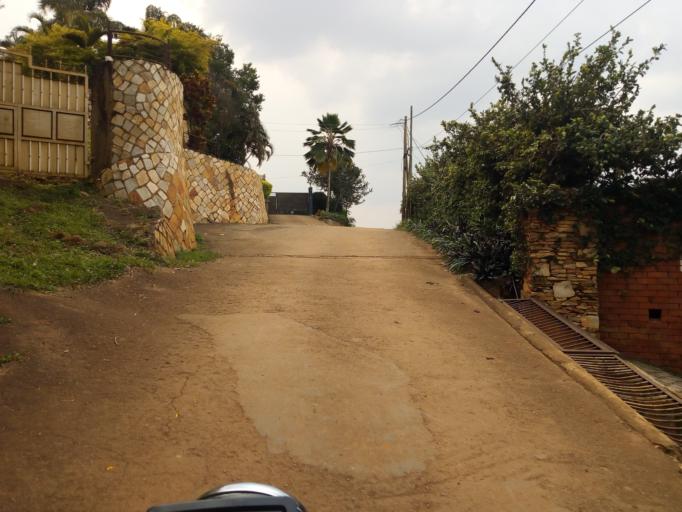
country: UG
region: Central Region
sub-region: Wakiso District
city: Kireka
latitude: 0.3263
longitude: 32.6325
